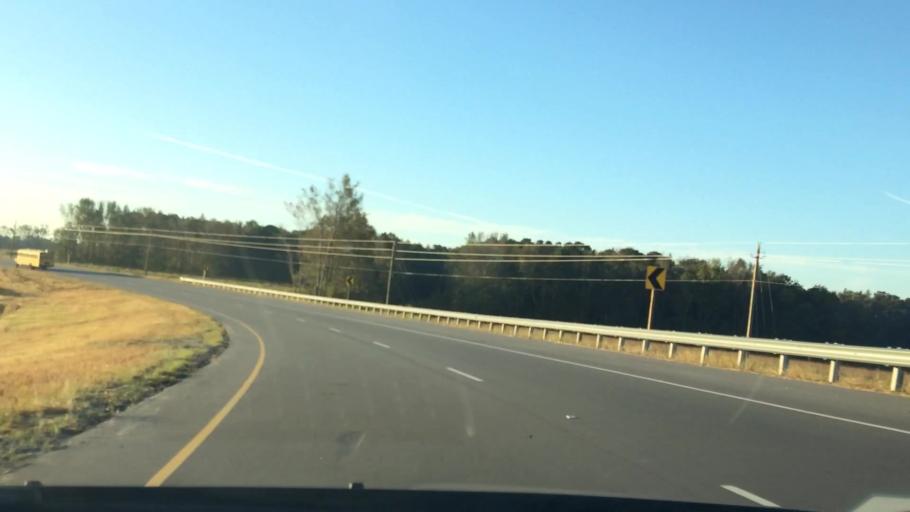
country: US
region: North Carolina
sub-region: Pitt County
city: Ayden
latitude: 35.4615
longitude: -77.4367
